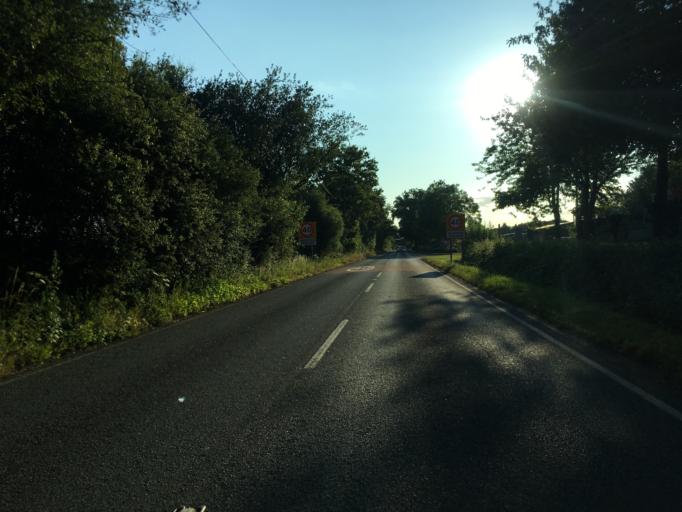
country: GB
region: England
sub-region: Hampshire
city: Tadley
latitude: 51.3612
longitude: -1.1753
